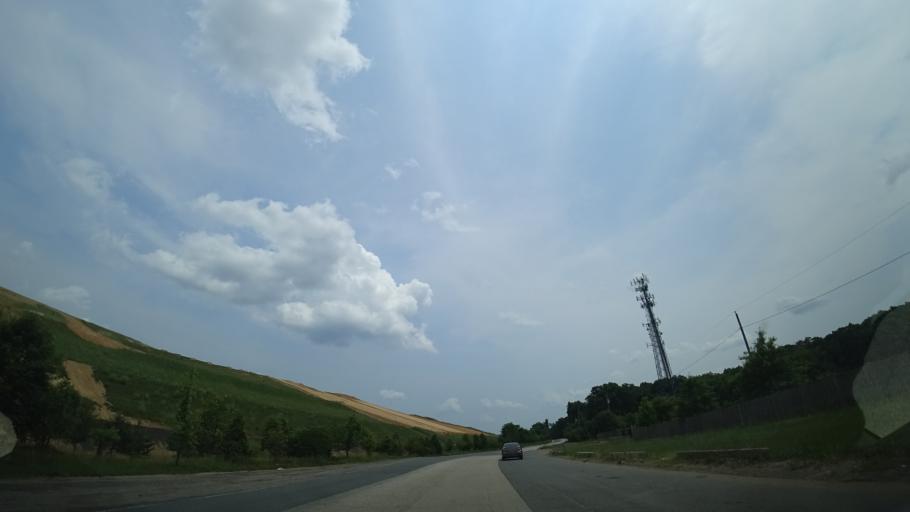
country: US
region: Virginia
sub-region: Fairfax County
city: Lorton
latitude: 38.6845
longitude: -77.2368
